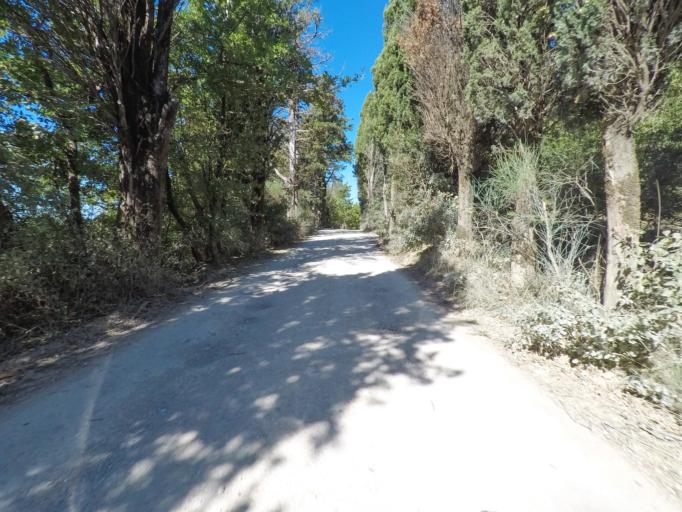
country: IT
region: Tuscany
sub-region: Provincia di Siena
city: Castellina in Chianti
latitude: 43.4331
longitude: 11.3330
